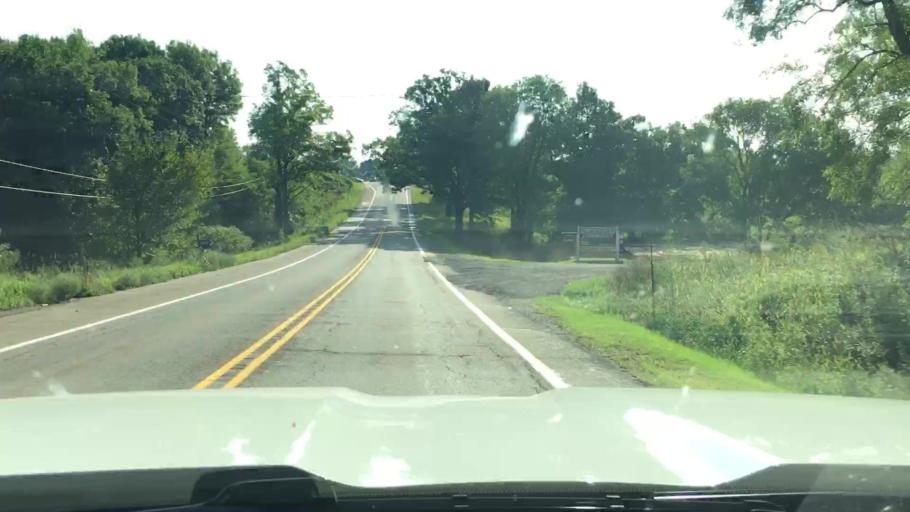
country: US
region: Michigan
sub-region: Kent County
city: Sparta
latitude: 43.2196
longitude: -85.6575
